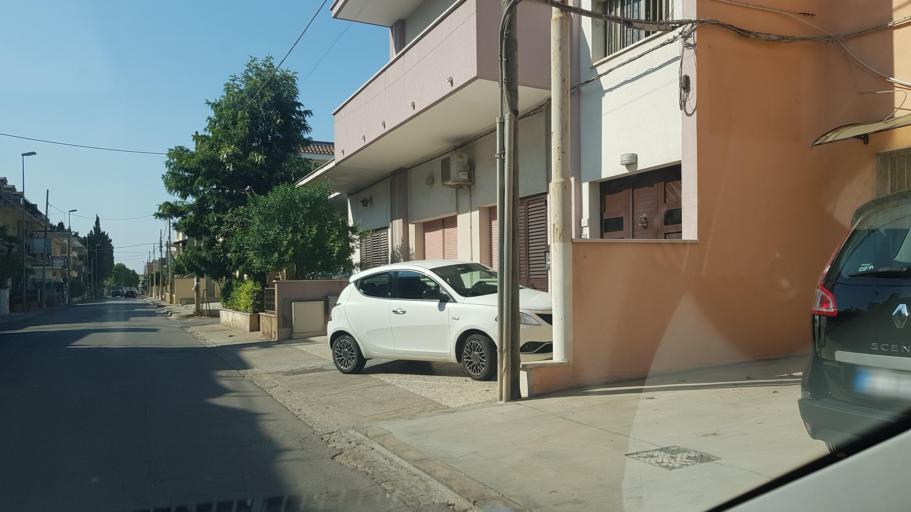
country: IT
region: Apulia
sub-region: Provincia di Lecce
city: Taurisano
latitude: 39.9501
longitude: 18.2181
